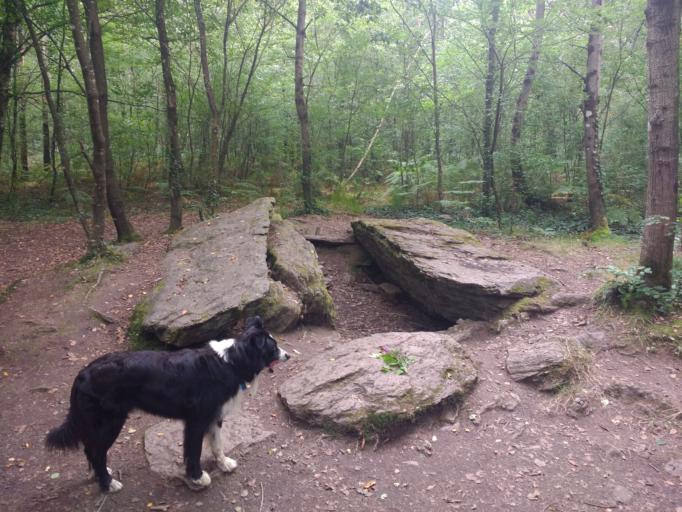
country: FR
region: Brittany
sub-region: Departement du Morbihan
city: Campeneac
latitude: 47.9919
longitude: -2.2691
